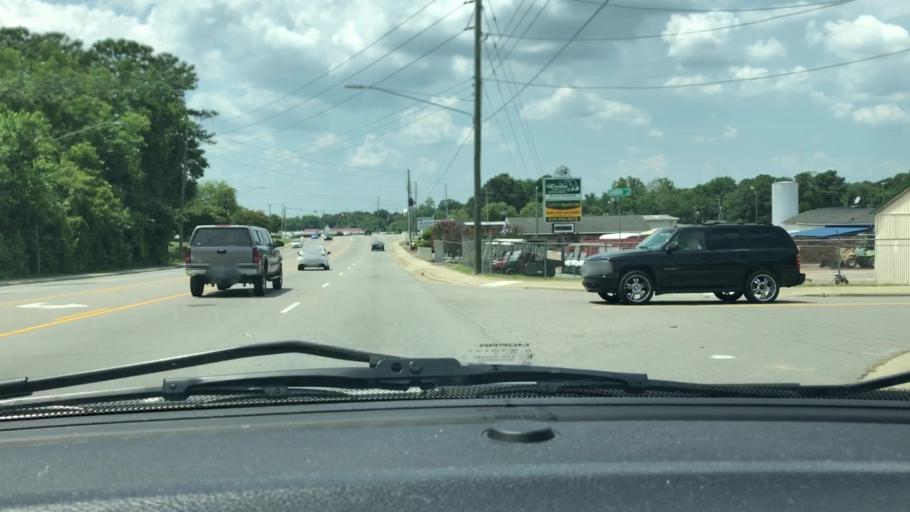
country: US
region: North Carolina
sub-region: Lee County
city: Sanford
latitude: 35.4691
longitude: -79.1646
